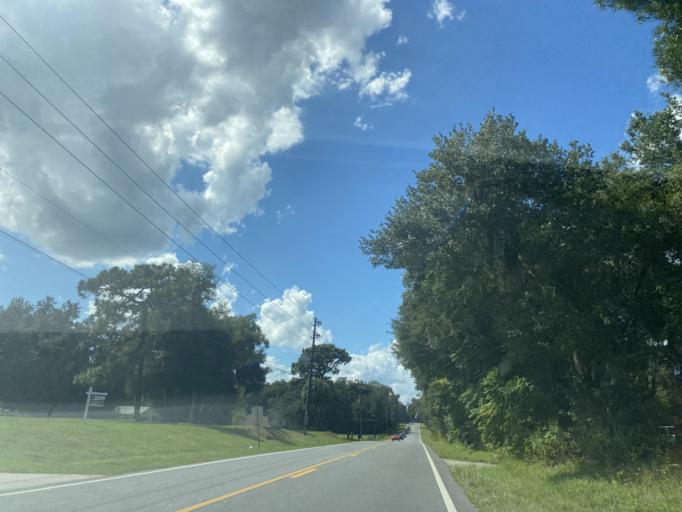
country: US
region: Florida
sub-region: Sumter County
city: The Villages
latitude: 28.9820
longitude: -81.9636
